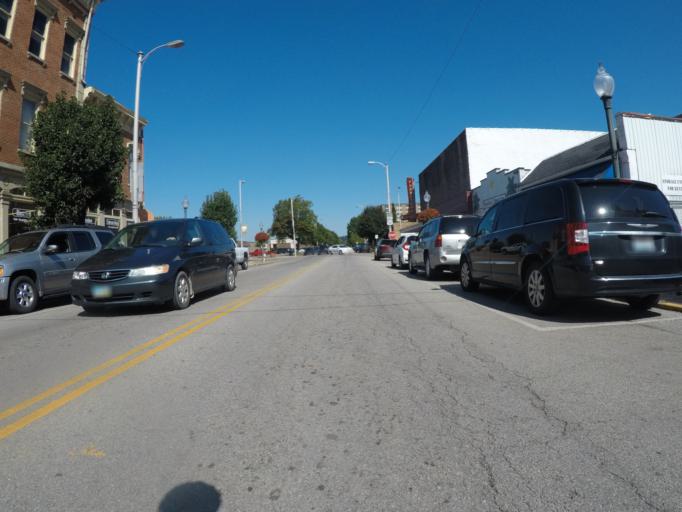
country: US
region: Ohio
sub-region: Lawrence County
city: Ironton
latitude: 38.5347
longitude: -82.6860
